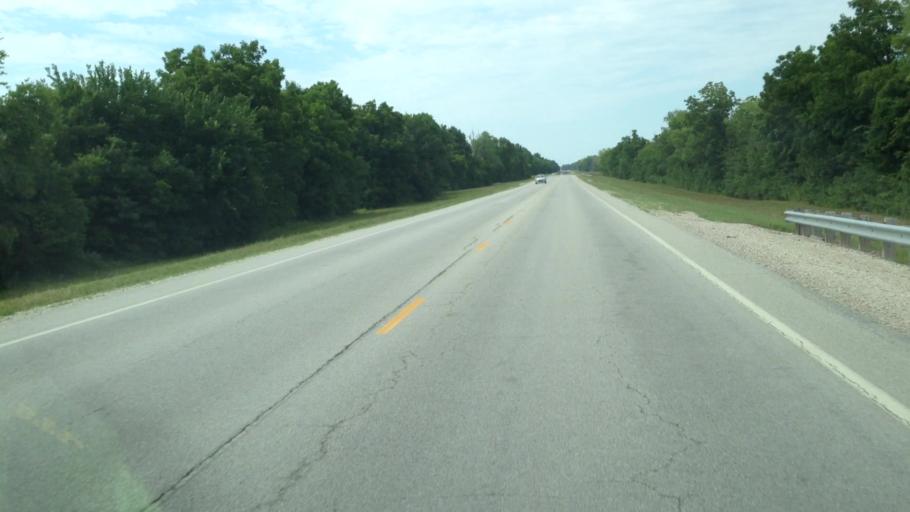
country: US
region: Kansas
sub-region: Labette County
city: Chetopa
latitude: 37.0571
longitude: -95.1026
